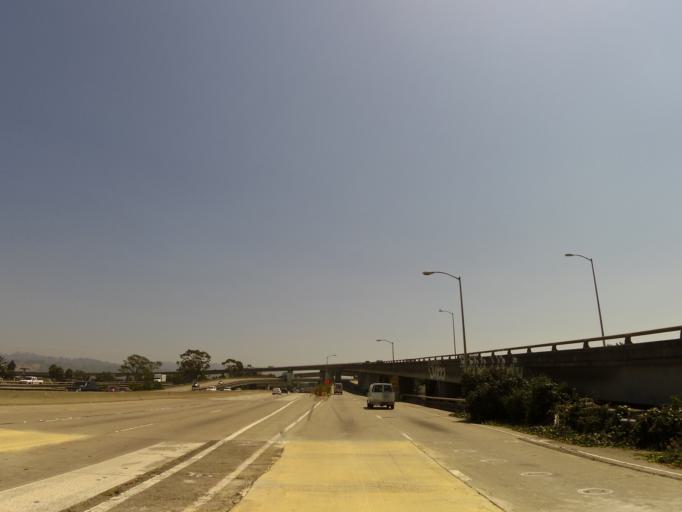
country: US
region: California
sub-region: Alameda County
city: Emeryville
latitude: 37.8252
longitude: -122.2728
